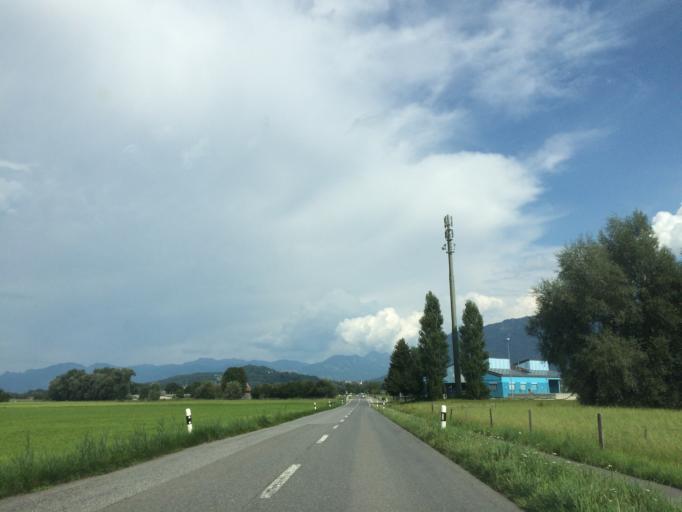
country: CH
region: Saint Gallen
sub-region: Wahlkreis Werdenberg
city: Haag (Rheintal)
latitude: 47.2069
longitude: 9.4657
